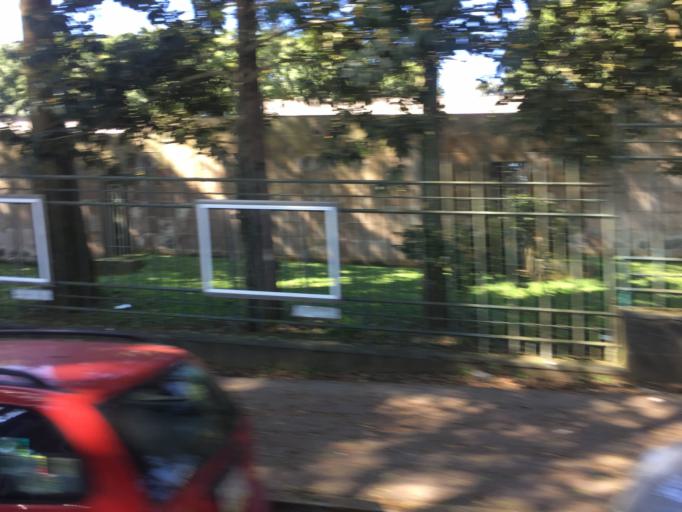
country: MX
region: Veracruz
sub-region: Xalapa
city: Xalapa de Enriquez
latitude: 19.5500
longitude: -96.9314
